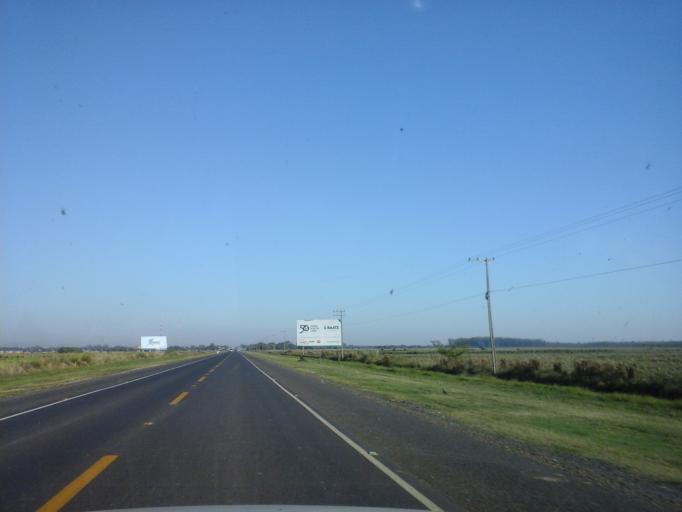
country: PY
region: Neembucu
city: Pilar
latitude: -26.8432
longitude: -58.2683
